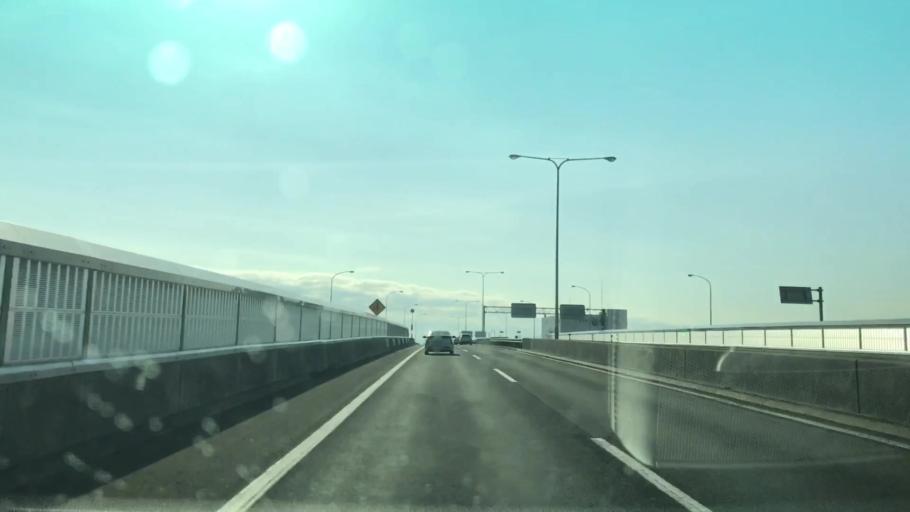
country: JP
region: Hokkaido
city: Sapporo
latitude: 43.0757
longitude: 141.4210
